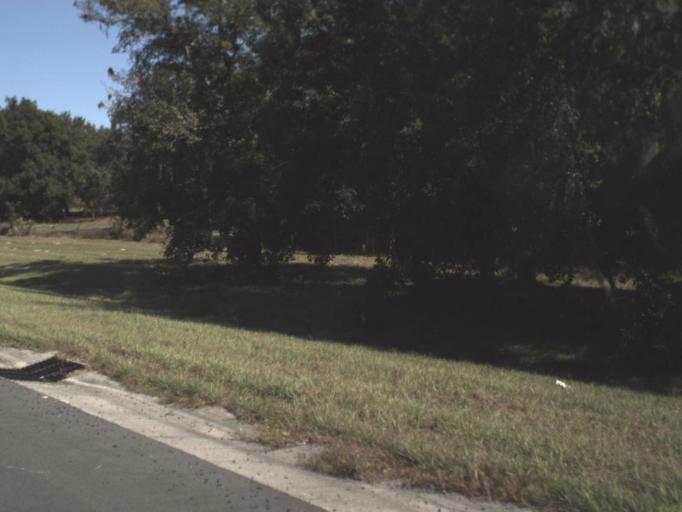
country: US
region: Florida
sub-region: Hernando County
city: Brookridge
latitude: 28.6182
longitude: -82.4931
